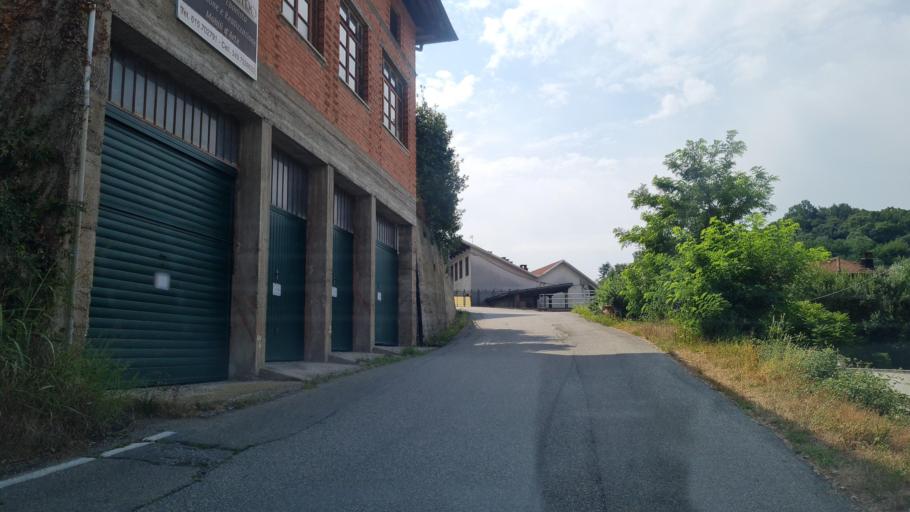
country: IT
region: Piedmont
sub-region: Provincia di Biella
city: Fontanella-Ozino
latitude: 45.6188
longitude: 8.1593
